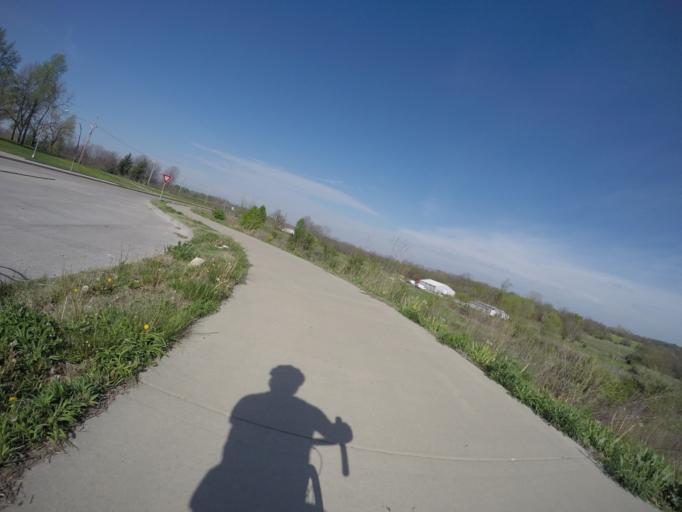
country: US
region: Missouri
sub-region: Cass County
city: Raymore
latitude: 38.8550
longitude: -94.4496
